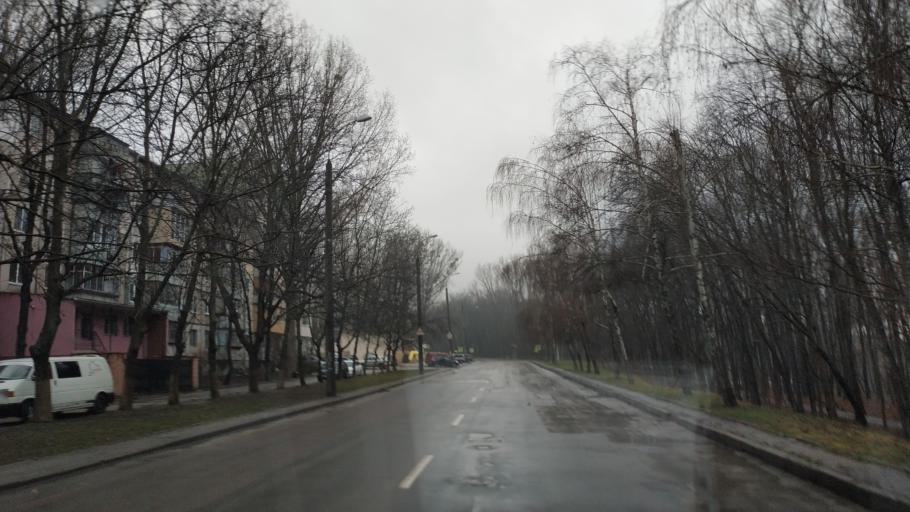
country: MD
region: Chisinau
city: Vatra
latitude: 47.0385
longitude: 28.7815
